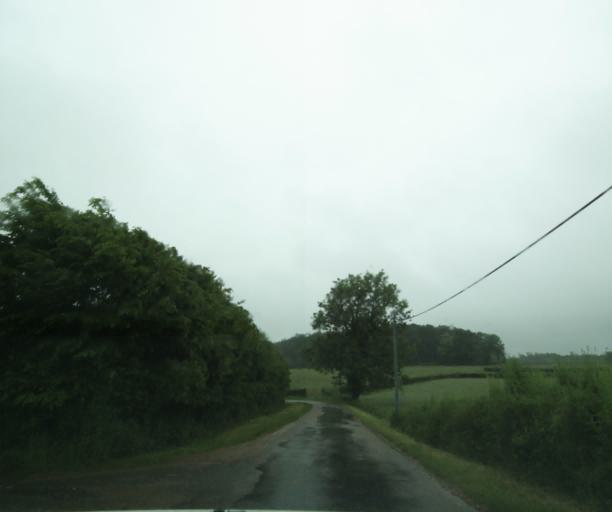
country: FR
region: Bourgogne
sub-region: Departement de Saone-et-Loire
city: Charolles
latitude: 46.4031
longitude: 4.2561
